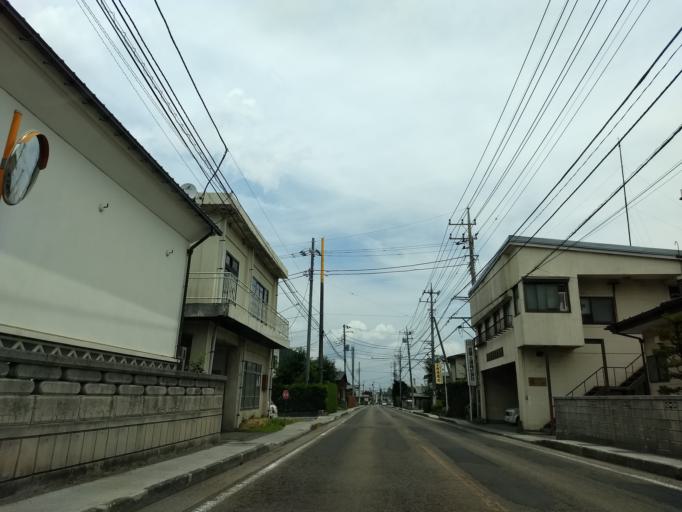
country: JP
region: Yamanashi
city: Fujikawaguchiko
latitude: 35.5006
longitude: 138.8135
